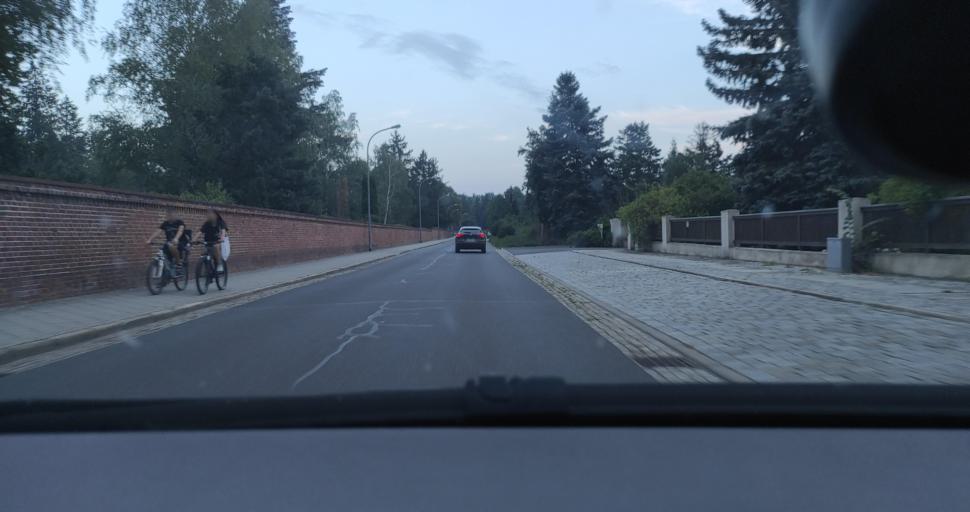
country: DE
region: Brandenburg
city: Forst
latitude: 51.7586
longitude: 14.6402
